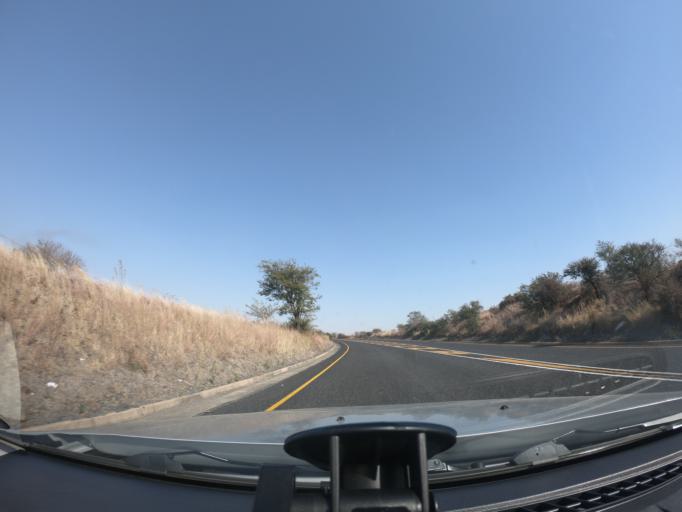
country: ZA
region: KwaZulu-Natal
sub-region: uThukela District Municipality
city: Ladysmith
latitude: -28.7060
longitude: 29.8182
